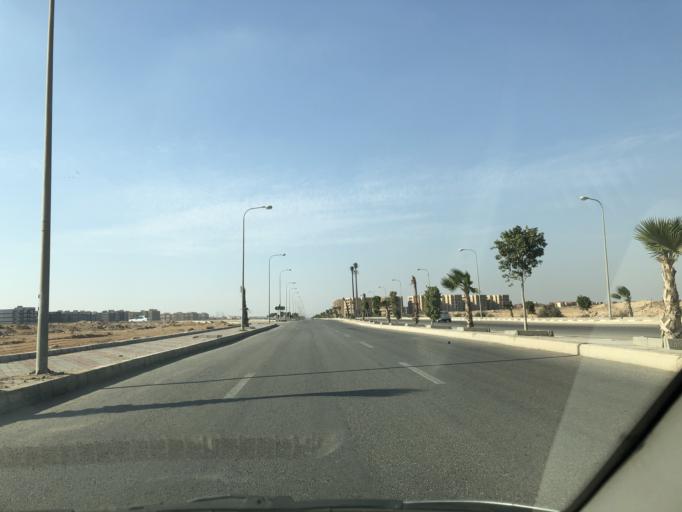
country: EG
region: Al Jizah
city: Madinat Sittah Uktubar
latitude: 29.9139
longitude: 31.0676
